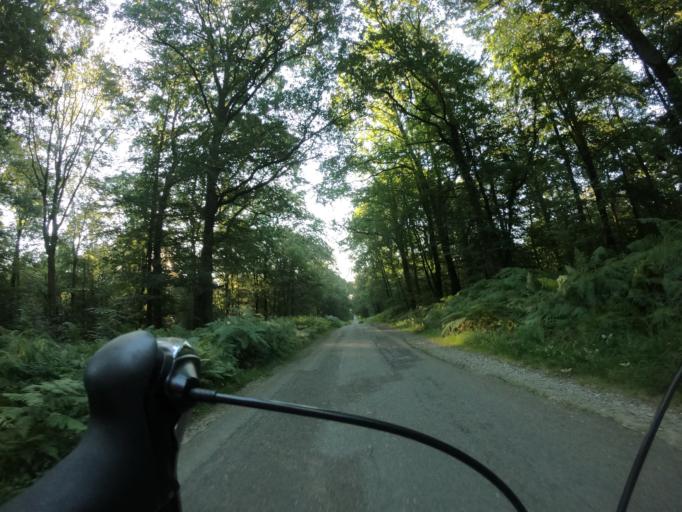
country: FR
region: Lower Normandy
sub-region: Departement de l'Orne
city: Magny-le-Desert
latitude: 48.5399
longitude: -0.3327
